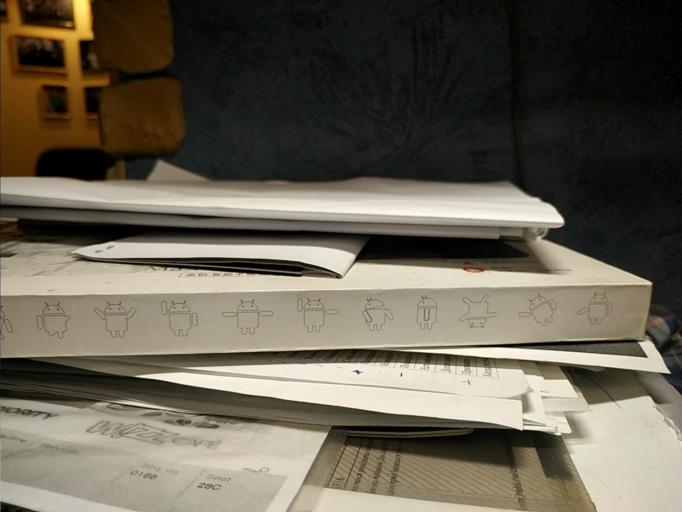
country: RU
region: Tverskaya
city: Zubtsov
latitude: 56.0802
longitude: 34.8023
